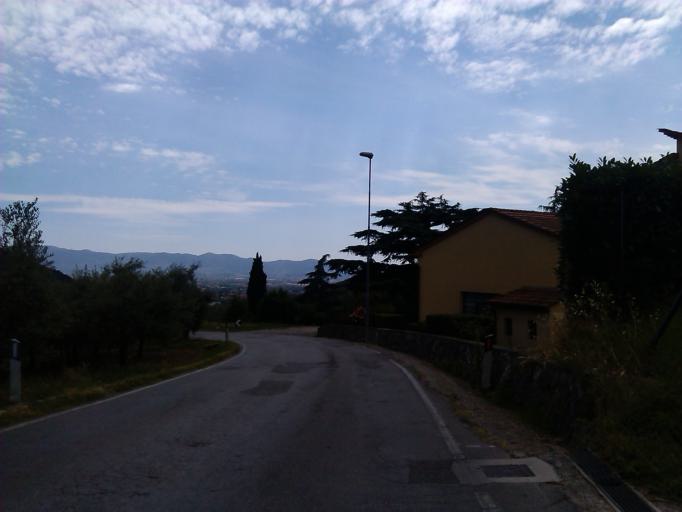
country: IT
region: Tuscany
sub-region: Provincia di Prato
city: Montemurlo
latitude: 43.9574
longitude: 11.0415
